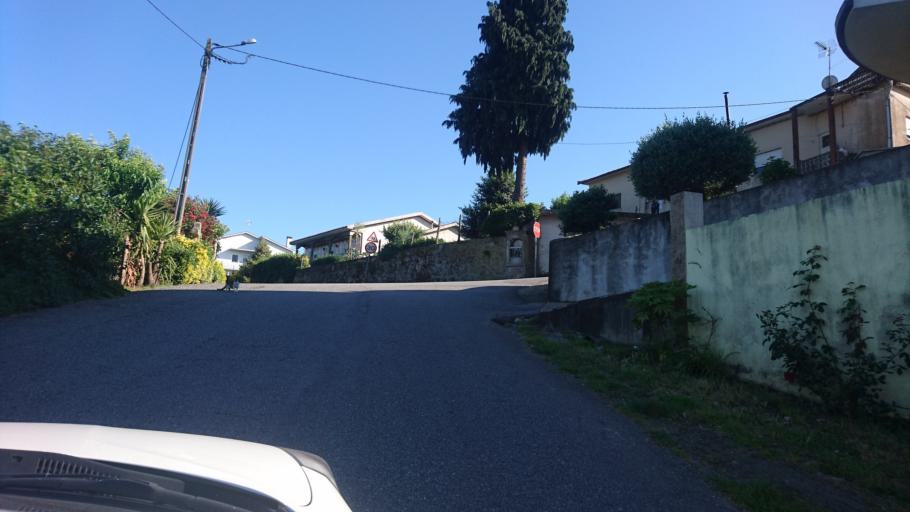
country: PT
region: Porto
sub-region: Paredes
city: Recarei
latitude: 41.1478
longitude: -8.3882
